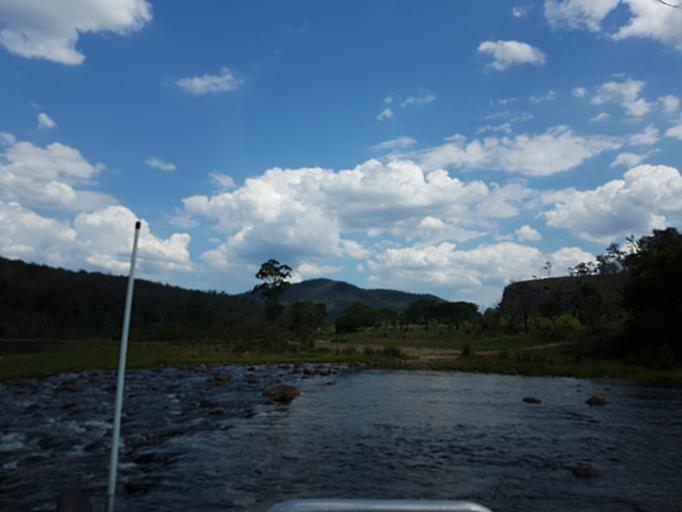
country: AU
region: Victoria
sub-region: East Gippsland
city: Lakes Entrance
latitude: -37.3964
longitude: 148.3354
